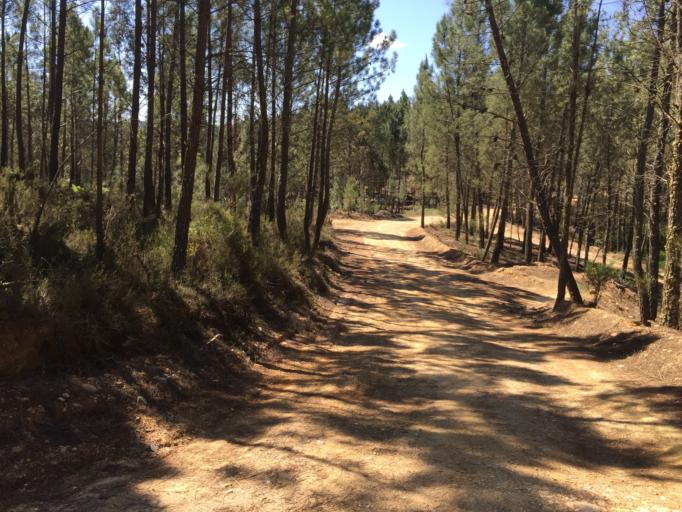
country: PT
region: Coimbra
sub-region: Pampilhosa da Serra
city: Pampilhosa da Serra
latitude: 40.0773
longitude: -7.7793
